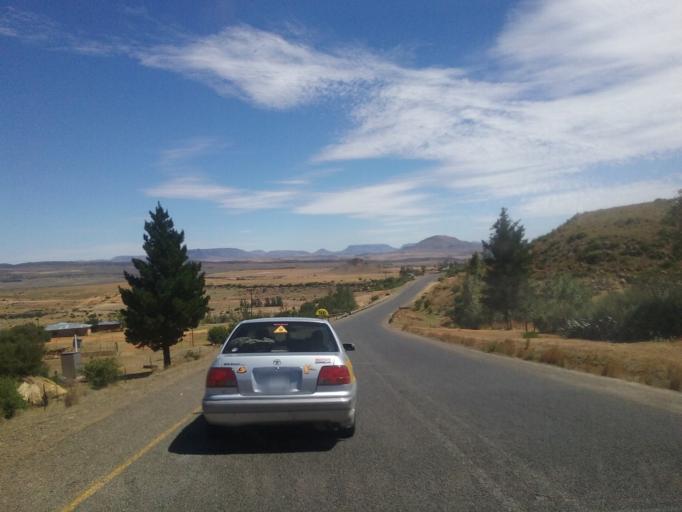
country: LS
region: Mohale's Hoek District
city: Mohale's Hoek
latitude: -30.1989
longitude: 27.4163
